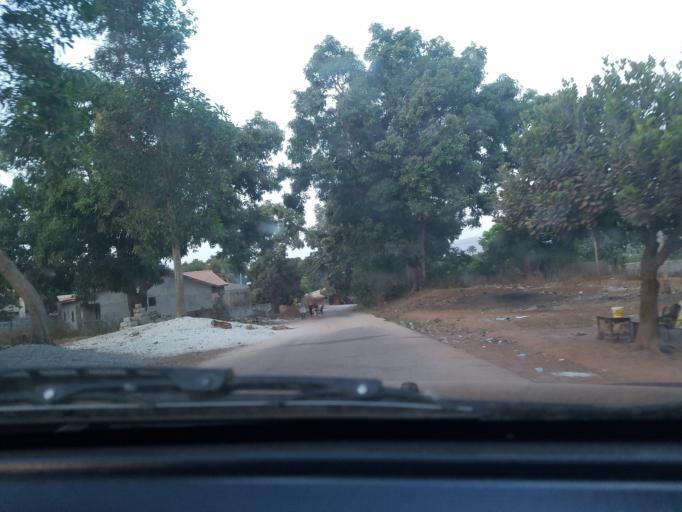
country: GN
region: Kindia
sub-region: Prefecture de Dubreka
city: Dubreka
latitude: 9.7885
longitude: -13.5153
